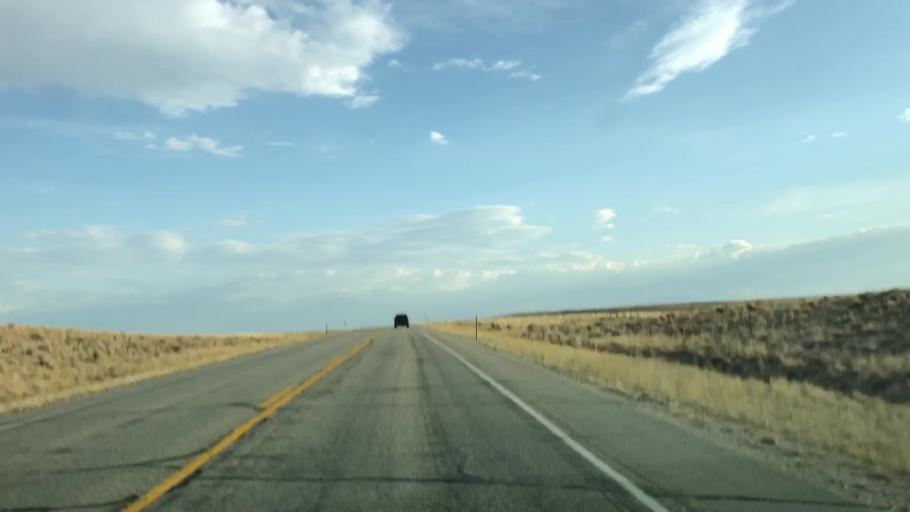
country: US
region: Wyoming
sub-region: Sublette County
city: Pinedale
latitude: 42.3442
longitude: -109.5219
